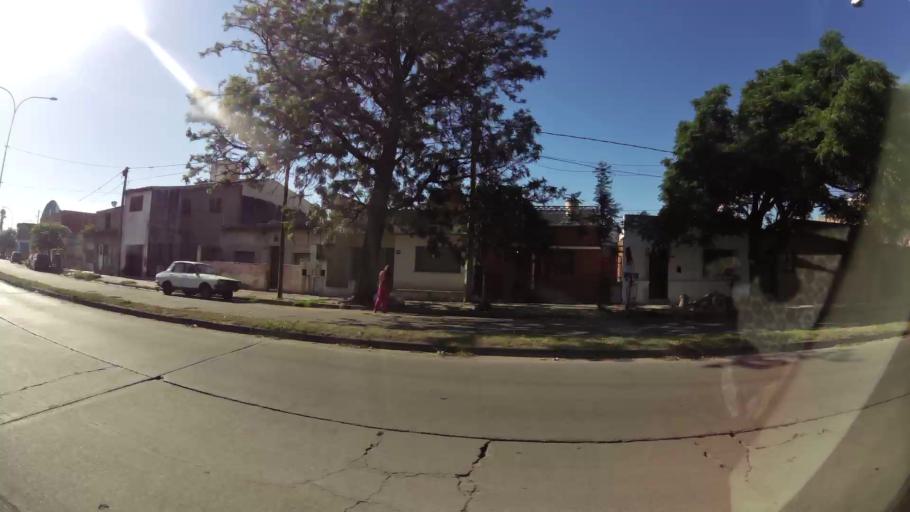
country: AR
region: Cordoba
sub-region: Departamento de Capital
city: Cordoba
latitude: -31.4223
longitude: -64.1602
